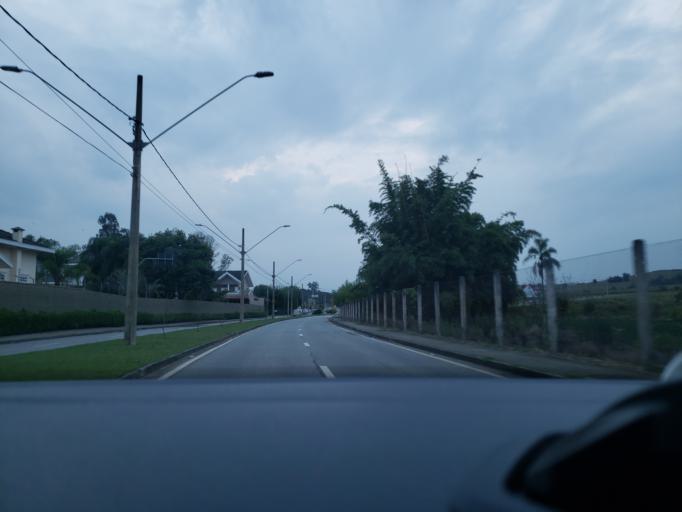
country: BR
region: Sao Paulo
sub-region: Sao Jose Dos Campos
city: Sao Jose dos Campos
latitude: -23.1968
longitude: -45.9433
